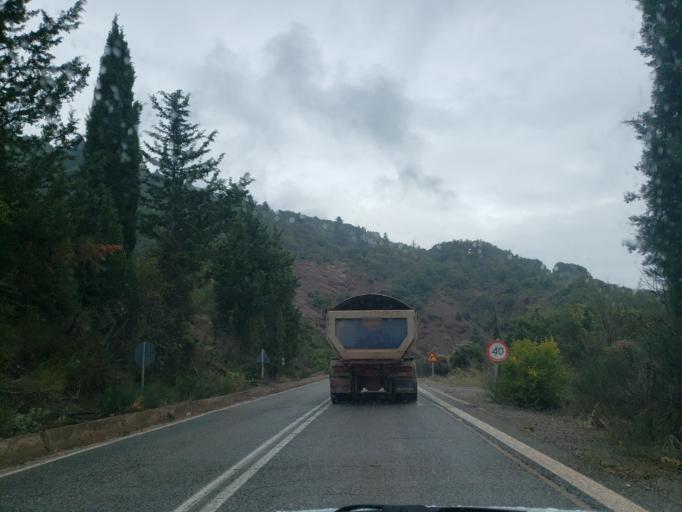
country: GR
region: Central Greece
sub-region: Nomos Fokidos
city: Amfissa
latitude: 38.5828
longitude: 22.3927
